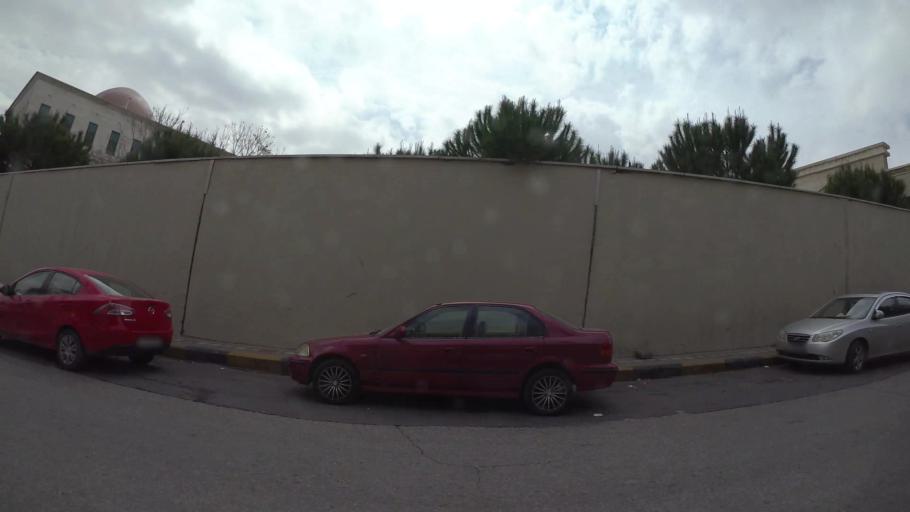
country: JO
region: Amman
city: Amman
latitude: 31.9600
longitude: 35.9541
